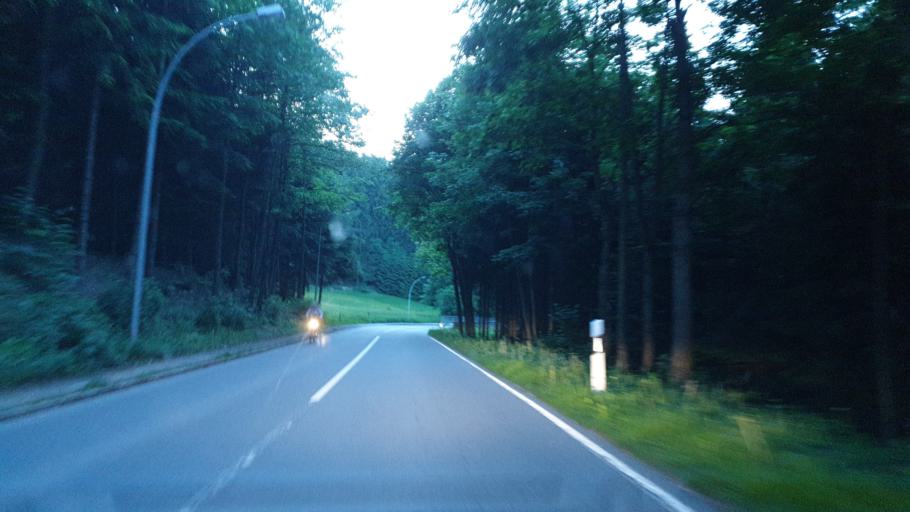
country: DE
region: Saxony
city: Zschorlau
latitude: 50.5811
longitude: 12.6590
